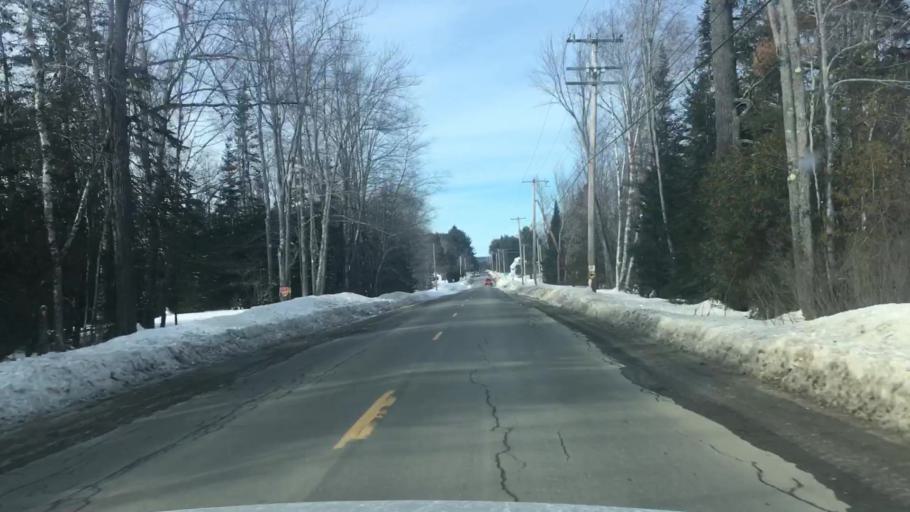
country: US
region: Maine
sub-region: Penobscot County
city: Charleston
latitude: 45.0496
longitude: -69.0297
